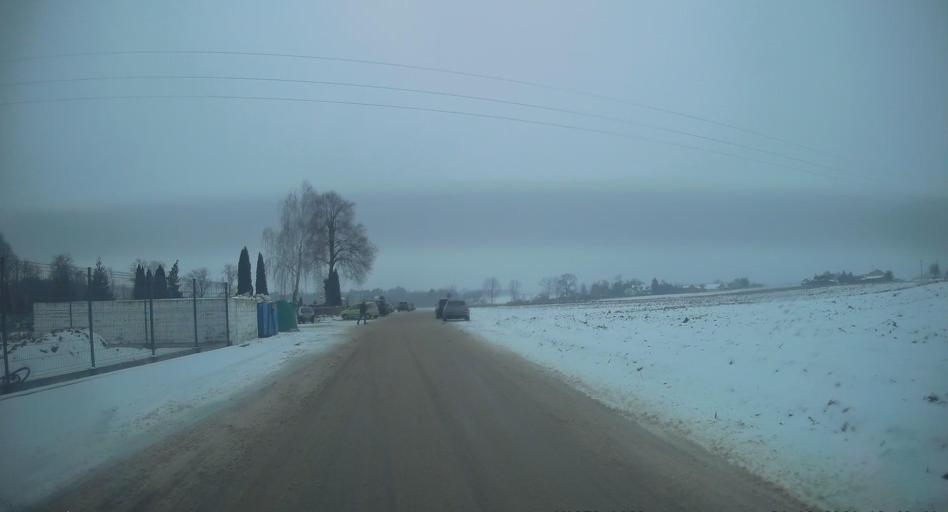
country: PL
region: Lodz Voivodeship
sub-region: Powiat tomaszowski
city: Czerniewice
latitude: 51.6780
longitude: 20.2176
